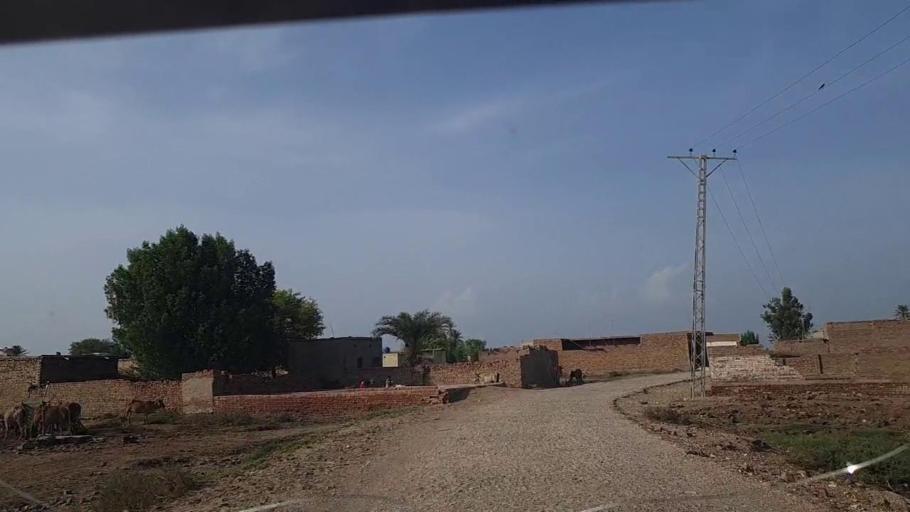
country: PK
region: Sindh
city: Ghotki
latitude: 28.0131
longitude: 69.2938
